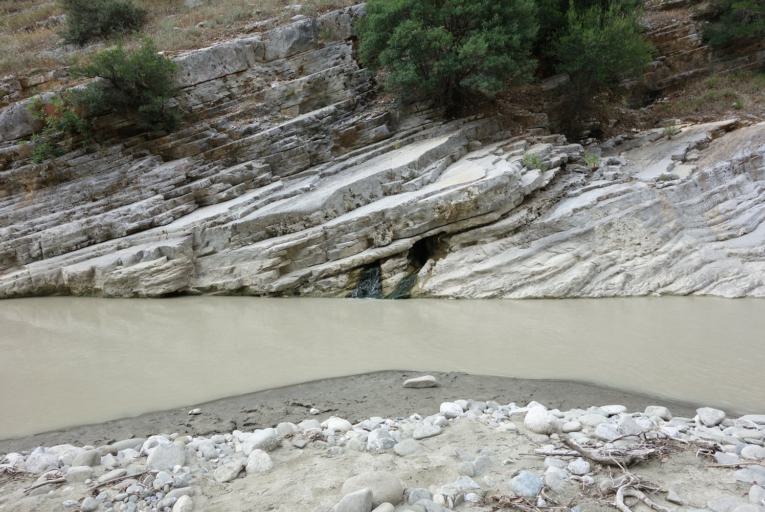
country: AL
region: Gjirokaster
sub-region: Rrethi i Permetit
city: Petran
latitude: 40.2447
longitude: 20.4335
